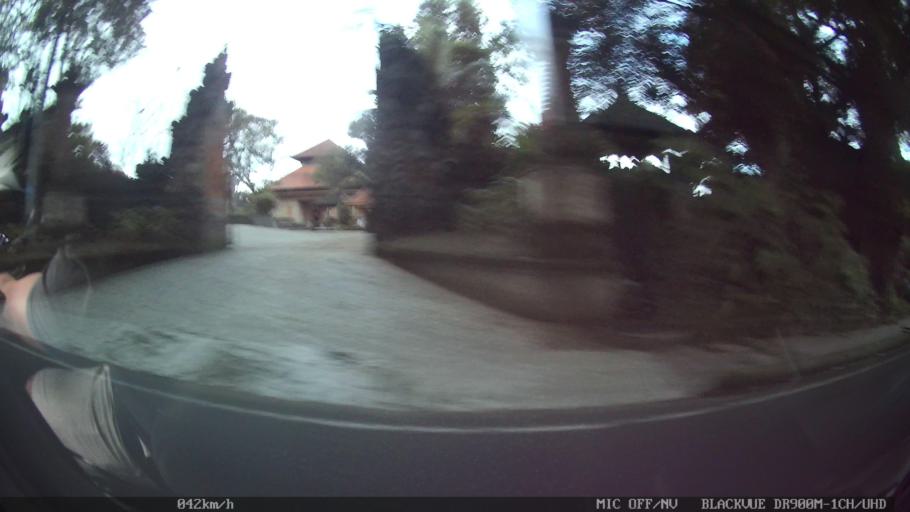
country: ID
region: Bali
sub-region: Kabupaten Gianyar
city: Ubud
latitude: -8.4933
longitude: 115.2535
